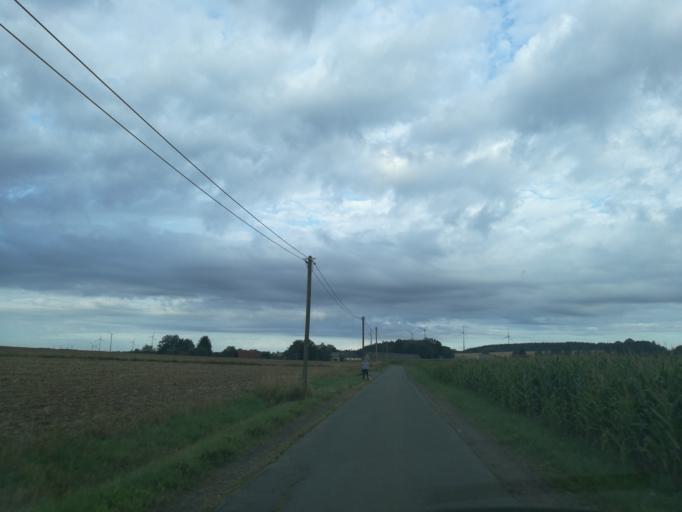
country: DE
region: Bavaria
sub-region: Upper Franconia
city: Regnitzlosau
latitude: 50.3235
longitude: 12.0745
